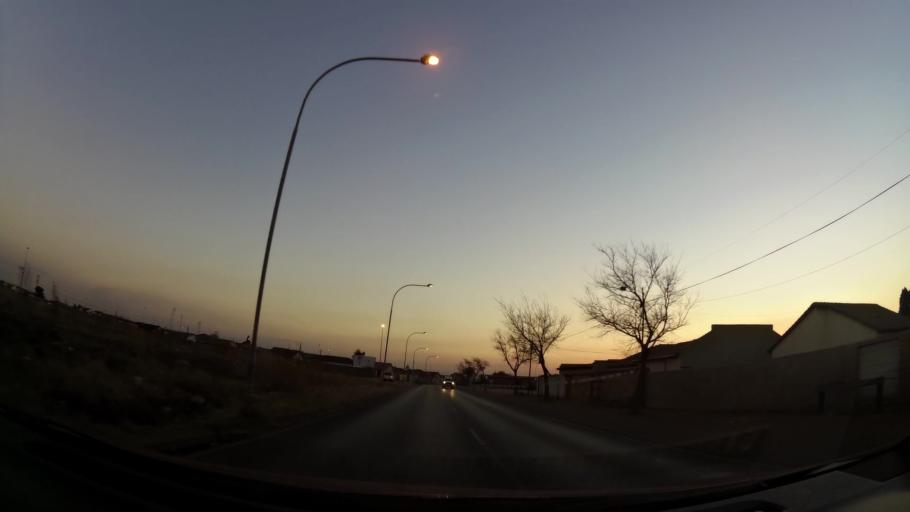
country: ZA
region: Gauteng
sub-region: City of Johannesburg Metropolitan Municipality
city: Soweto
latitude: -26.2336
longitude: 27.8306
